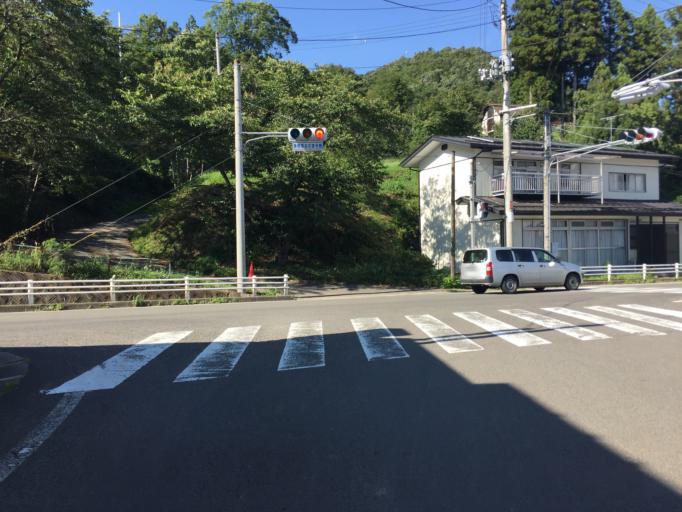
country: JP
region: Fukushima
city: Hobaramachi
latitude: 37.7681
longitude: 140.5796
